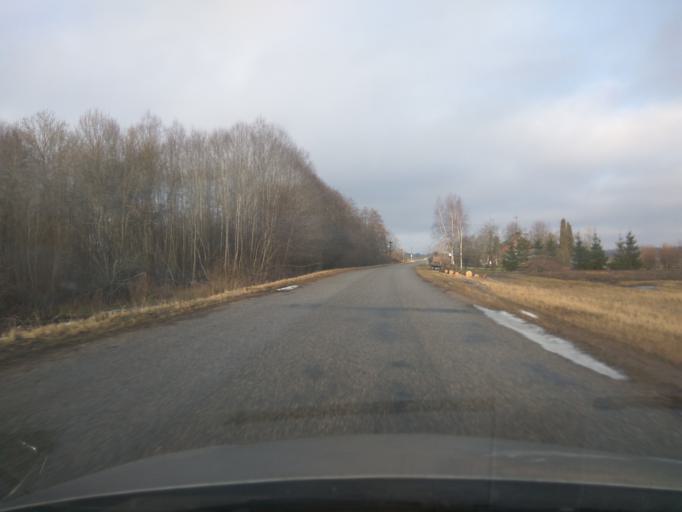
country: LV
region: Saldus Rajons
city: Saldus
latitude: 56.7616
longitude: 22.3855
